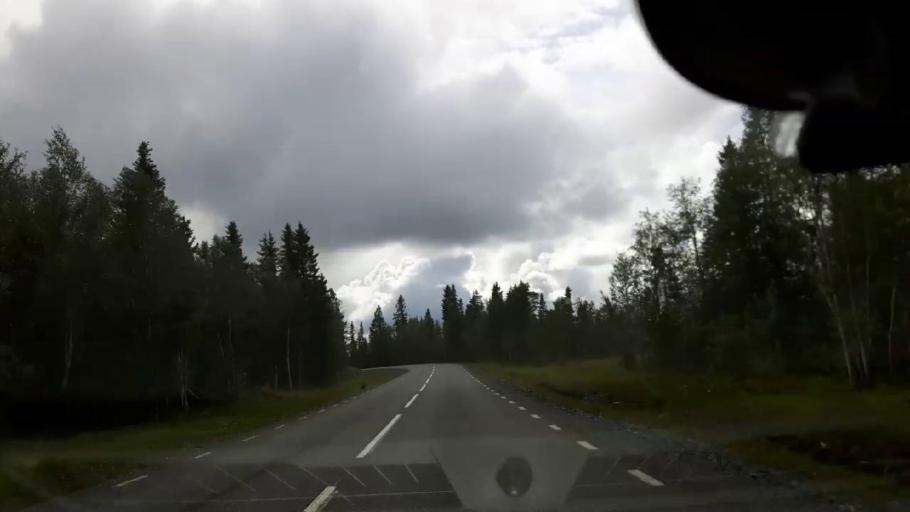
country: SE
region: Jaemtland
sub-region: Krokoms Kommun
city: Valla
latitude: 63.4652
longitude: 13.8271
